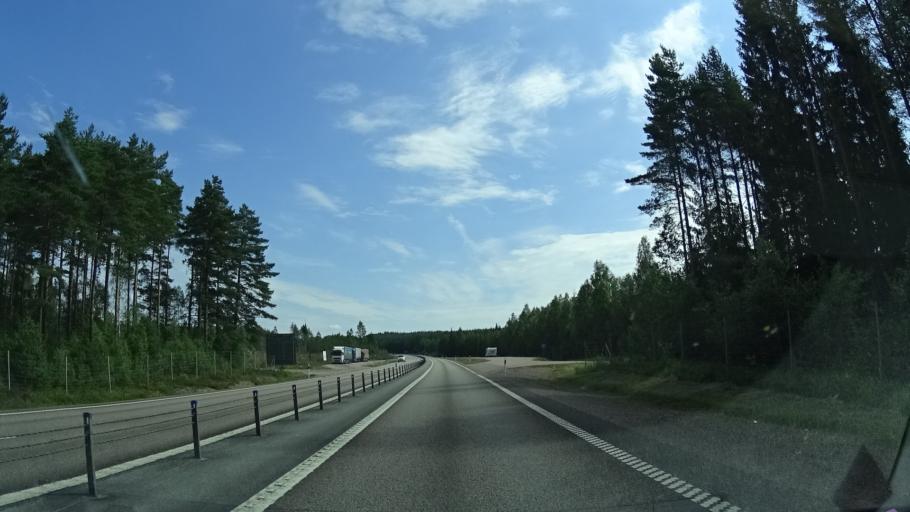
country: SE
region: Vaermland
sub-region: Kristinehamns Kommun
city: Bjorneborg
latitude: 59.3108
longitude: 14.1966
